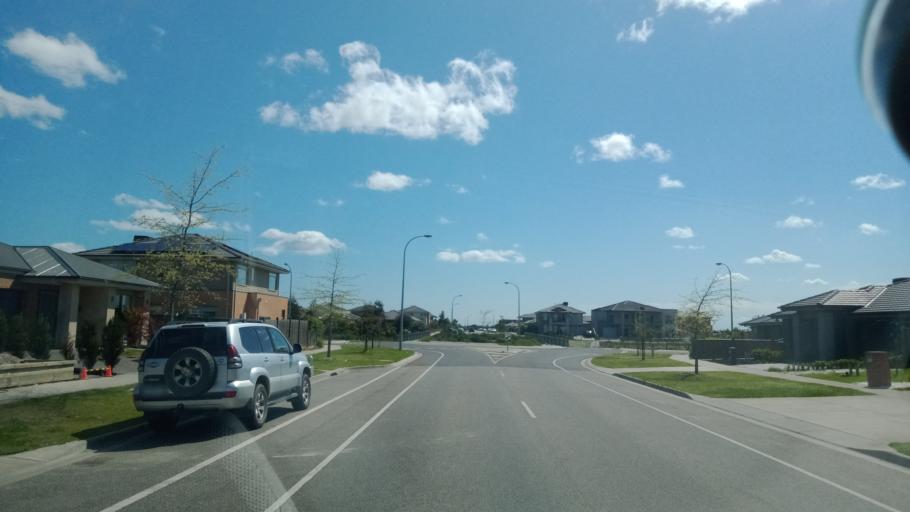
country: AU
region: Victoria
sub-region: Casey
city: Cranbourne West
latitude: -38.0979
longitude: 145.2505
